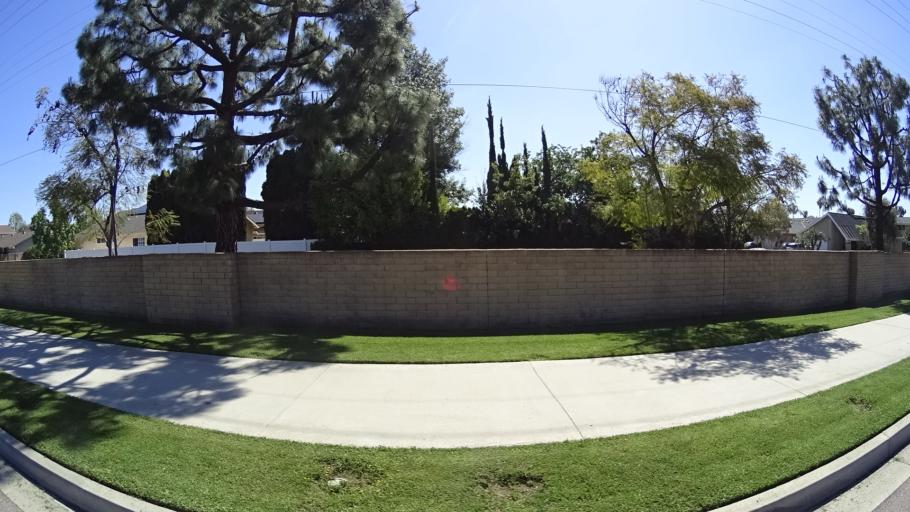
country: US
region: California
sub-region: Orange County
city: Villa Park
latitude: 33.8057
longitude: -117.8219
